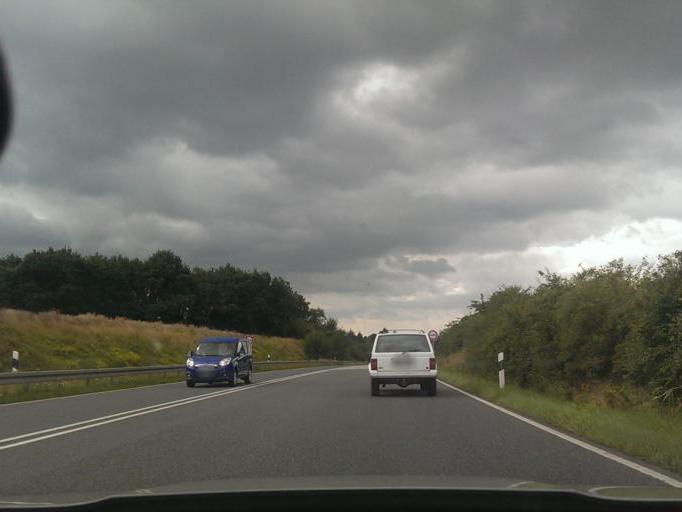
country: DE
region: Lower Saxony
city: Bevern
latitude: 51.8603
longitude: 9.5240
